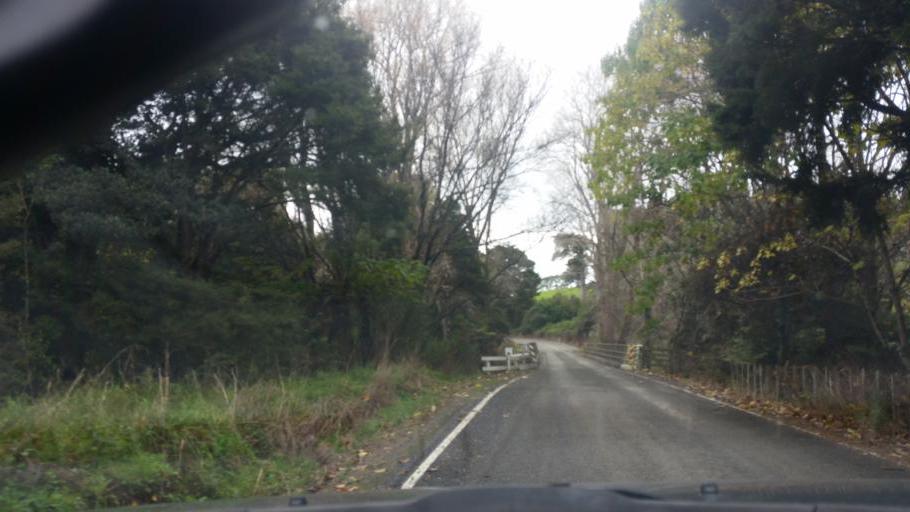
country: NZ
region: Northland
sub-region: Kaipara District
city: Dargaville
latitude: -35.7504
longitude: 173.9042
